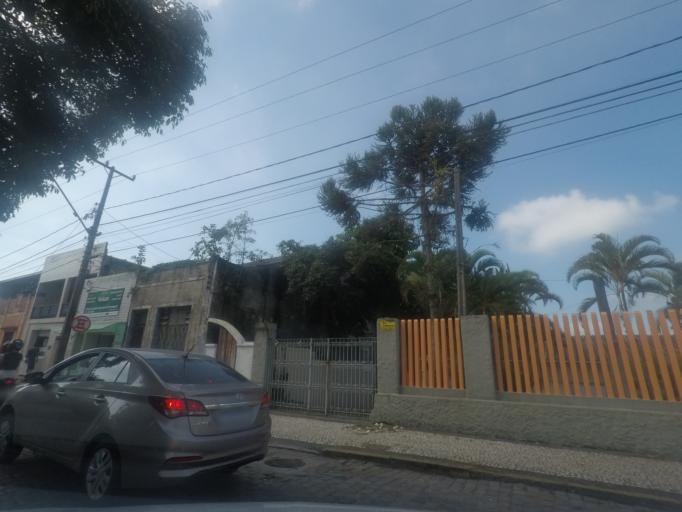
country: BR
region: Parana
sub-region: Paranagua
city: Paranagua
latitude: -25.5233
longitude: -48.5113
